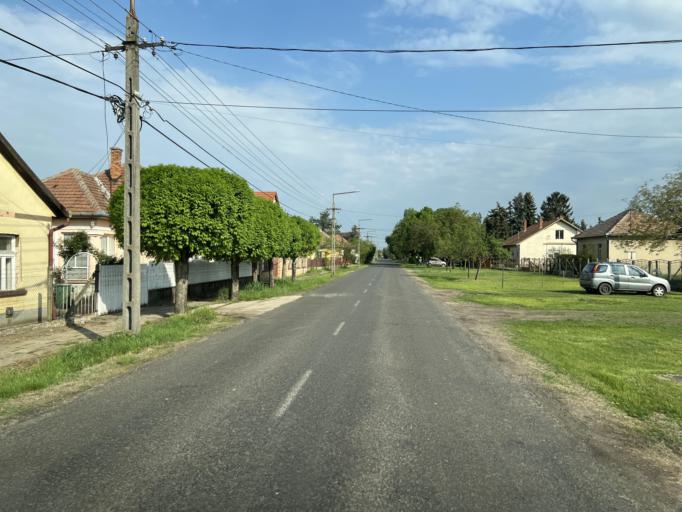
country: HU
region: Pest
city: Abony
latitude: 47.1754
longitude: 20.0153
